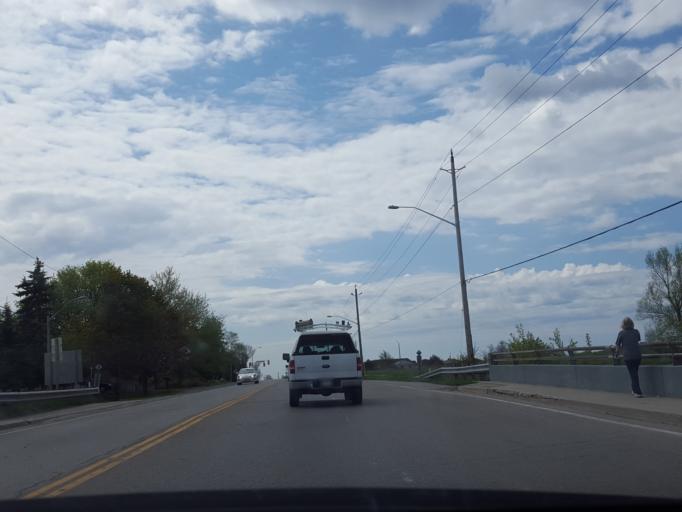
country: CA
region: Ontario
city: Oshawa
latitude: 43.9095
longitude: -78.7013
